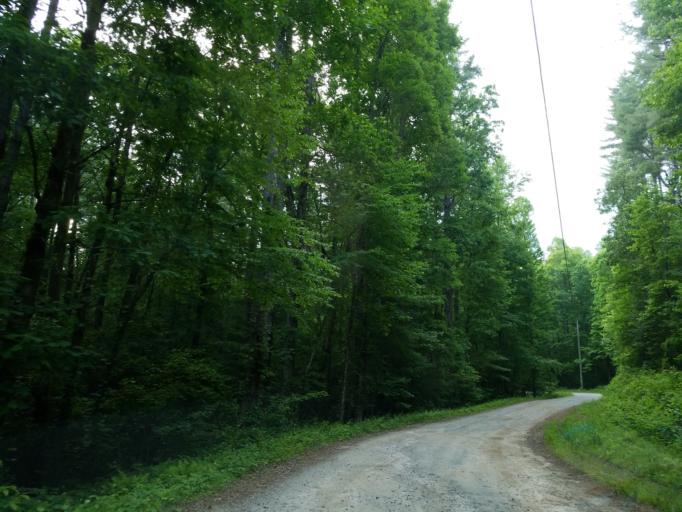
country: US
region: Georgia
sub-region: Lumpkin County
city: Dahlonega
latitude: 34.6012
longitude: -84.0936
